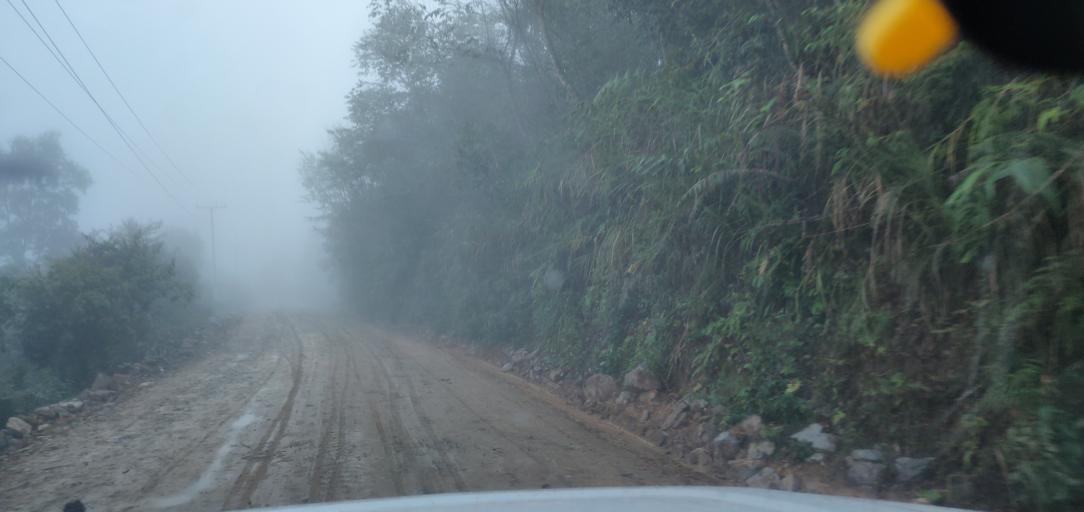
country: LA
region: Phongsali
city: Phongsali
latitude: 21.4251
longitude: 102.2560
